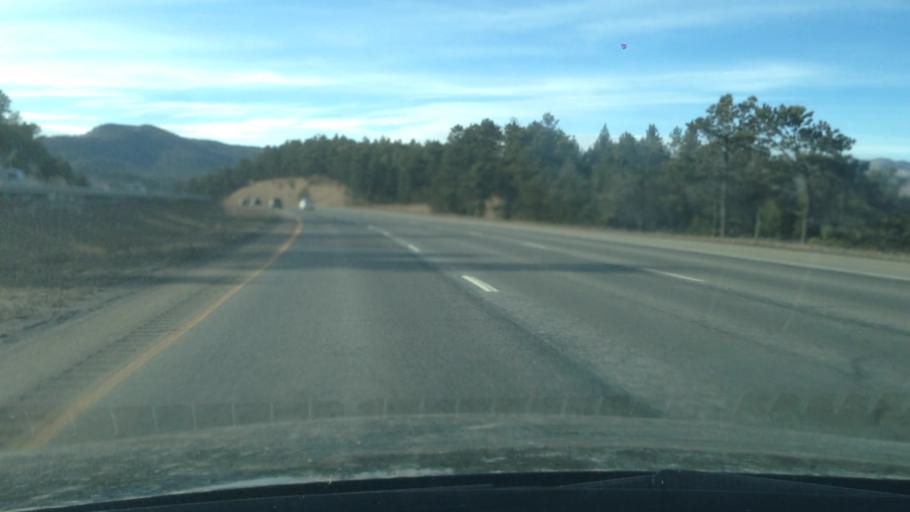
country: US
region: Colorado
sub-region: Jefferson County
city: Kittredge
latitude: 39.7107
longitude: -105.3508
